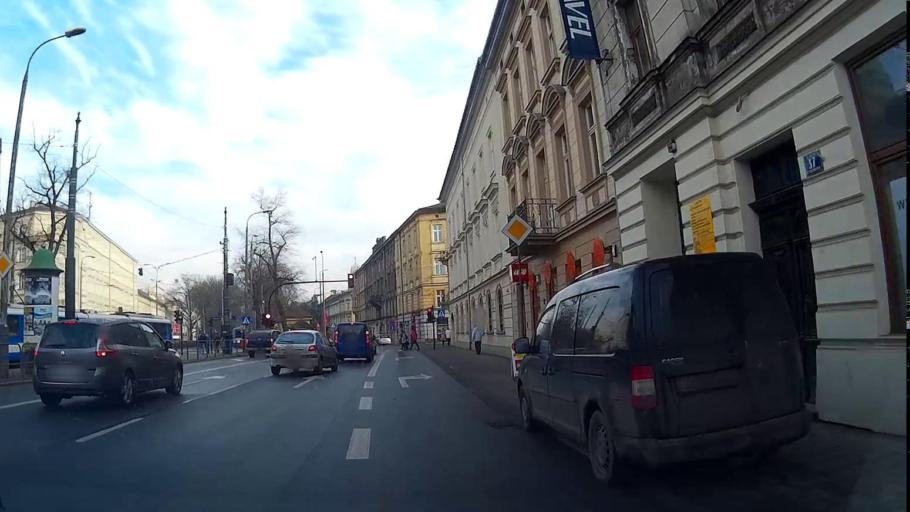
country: PL
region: Lesser Poland Voivodeship
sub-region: Krakow
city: Krakow
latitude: 50.0512
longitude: 19.9413
